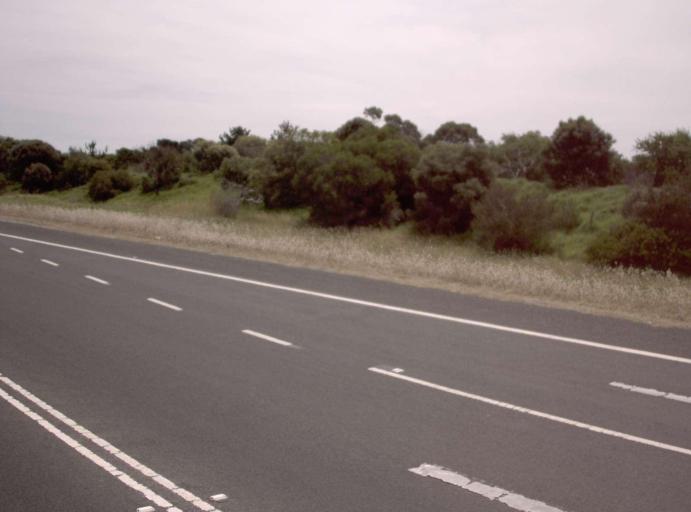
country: AU
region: Victoria
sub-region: Mornington Peninsula
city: Rosebud
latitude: -38.3706
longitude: 144.9075
